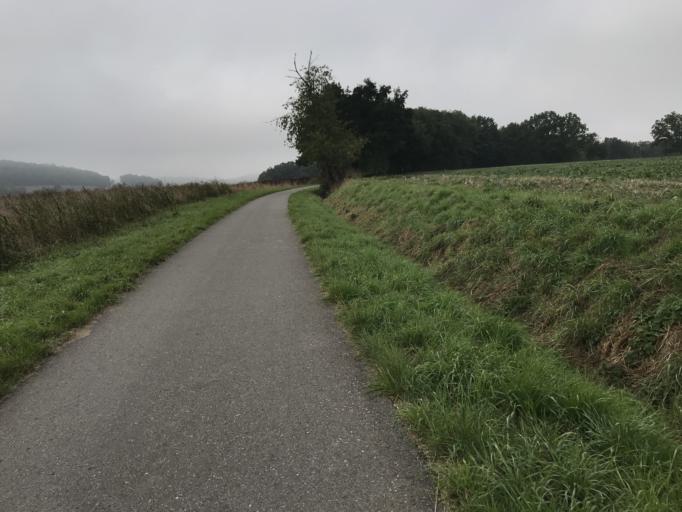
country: DE
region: Hesse
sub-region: Regierungsbezirk Kassel
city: Guxhagen
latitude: 51.1963
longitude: 9.4262
